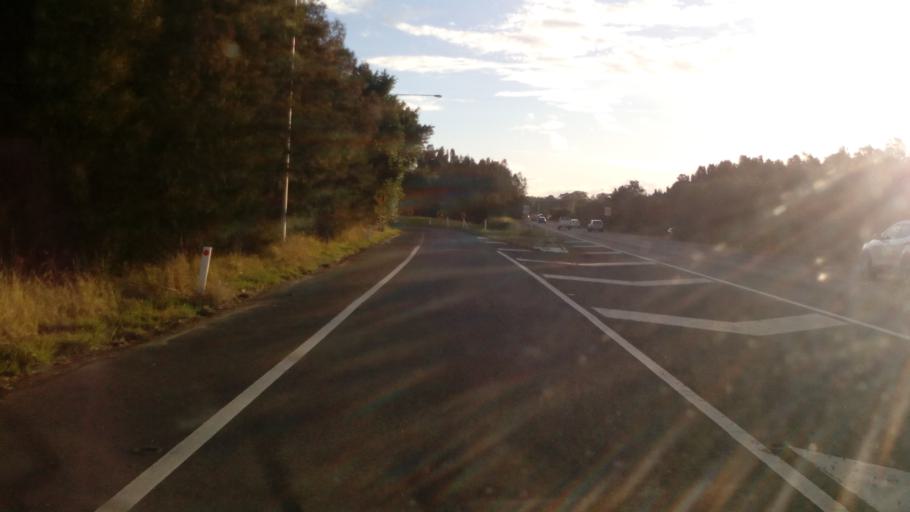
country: AU
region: New South Wales
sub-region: Newcastle
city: Beresfield
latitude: -32.8122
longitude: 151.6652
